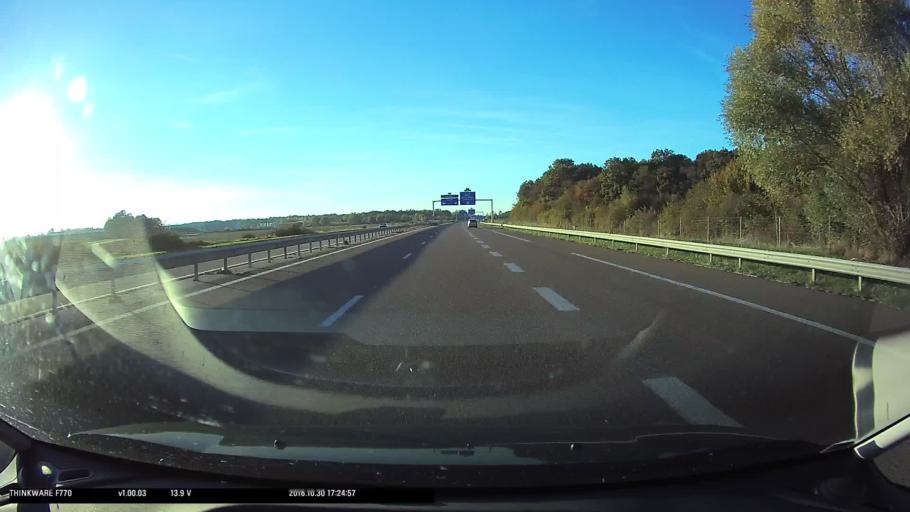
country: FR
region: Bourgogne
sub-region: Departement de la Cote-d'Or
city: Chevigny-Saint-Sauveur
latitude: 47.2716
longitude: 5.1556
